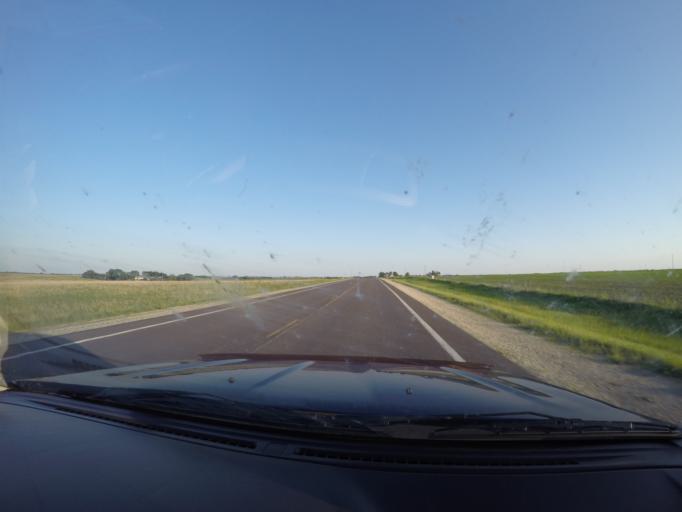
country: US
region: Kansas
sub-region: Marshall County
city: Blue Rapids
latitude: 39.6418
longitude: -96.7506
